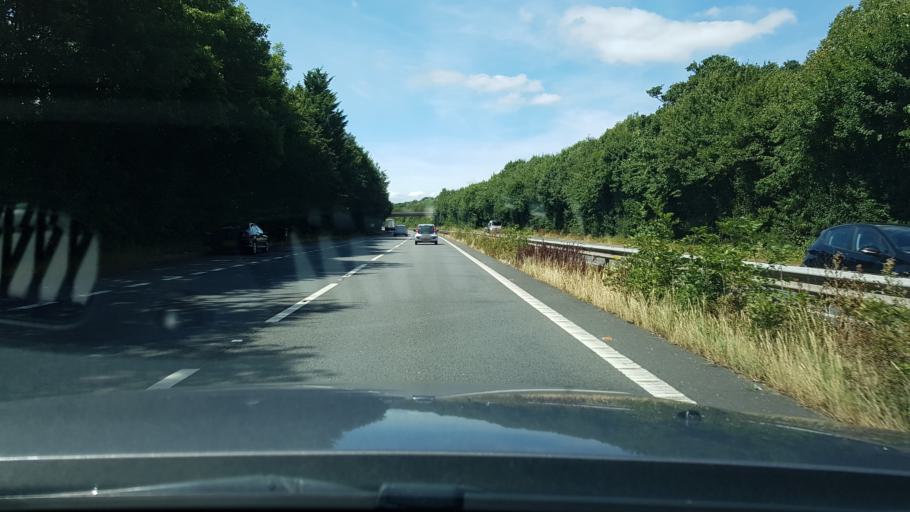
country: GB
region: England
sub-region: West Sussex
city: Bosham
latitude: 50.8558
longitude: -0.8761
